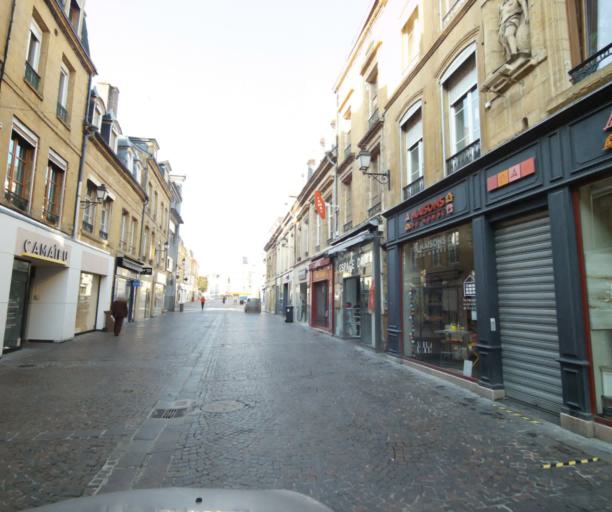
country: FR
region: Champagne-Ardenne
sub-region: Departement des Ardennes
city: Charleville-Mezieres
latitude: 49.7721
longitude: 4.7201
